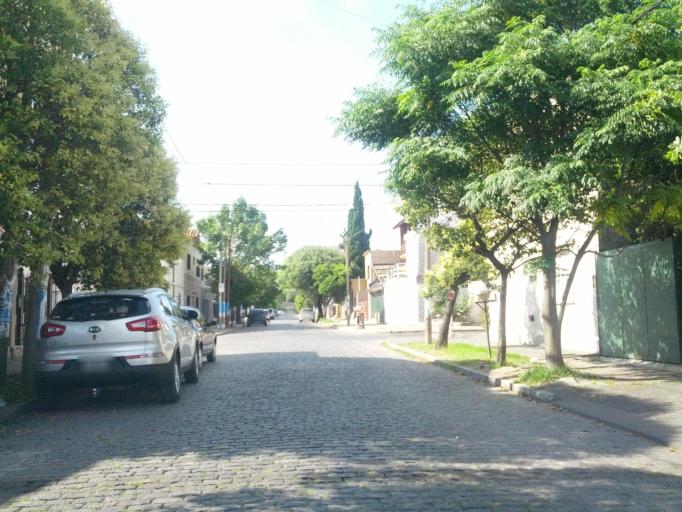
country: AR
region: Buenos Aires
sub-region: Partido de Moron
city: Moron
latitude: -34.6461
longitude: -58.5847
